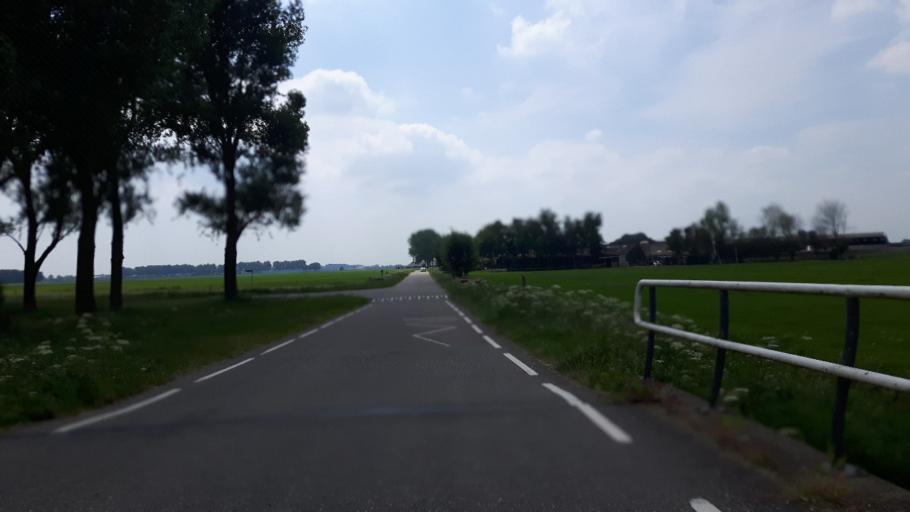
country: NL
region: Utrecht
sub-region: Gemeente Lopik
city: Lopik
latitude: 51.9257
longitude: 4.9520
